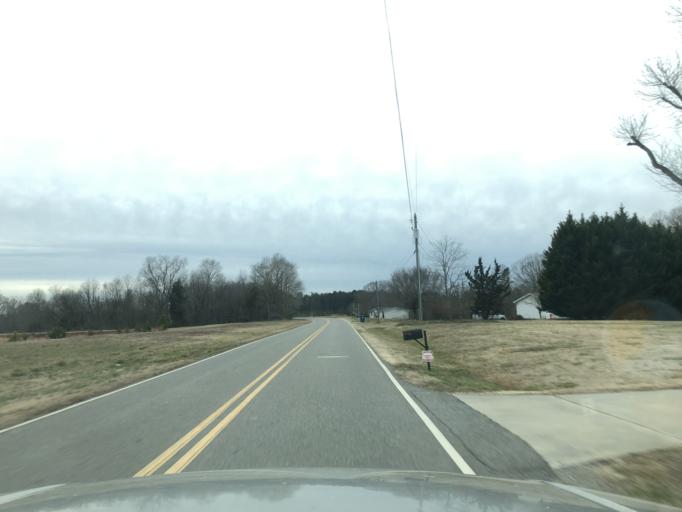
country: US
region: North Carolina
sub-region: Cleveland County
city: Shelby
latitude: 35.3415
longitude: -81.5303
